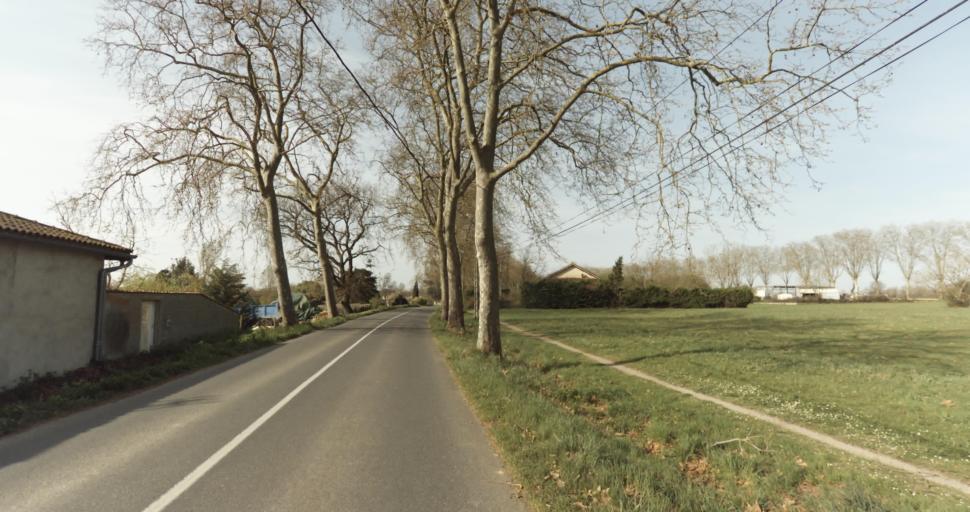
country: FR
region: Midi-Pyrenees
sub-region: Departement du Tarn
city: Saint-Sulpice-la-Pointe
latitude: 43.7760
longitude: 1.6690
